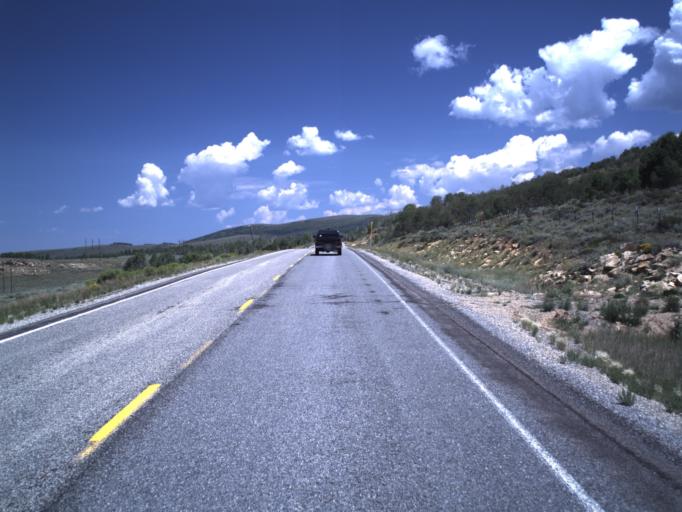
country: US
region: Utah
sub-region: Carbon County
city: Helper
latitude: 39.8445
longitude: -111.1285
